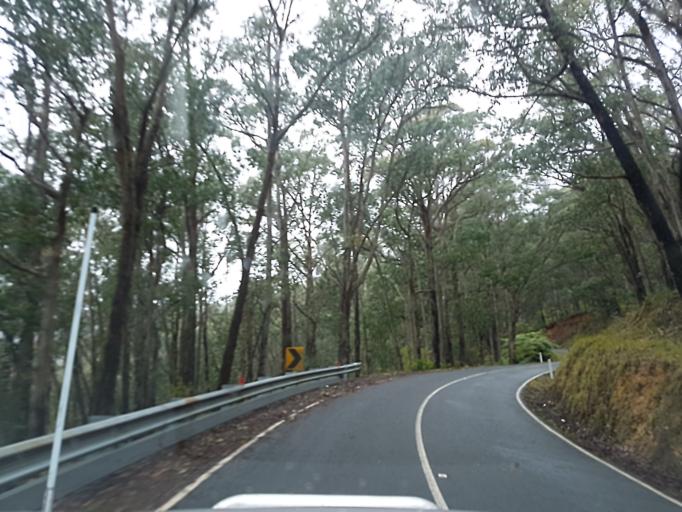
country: AU
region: Victoria
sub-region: Yarra Ranges
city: Millgrove
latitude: -37.6587
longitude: 145.8602
